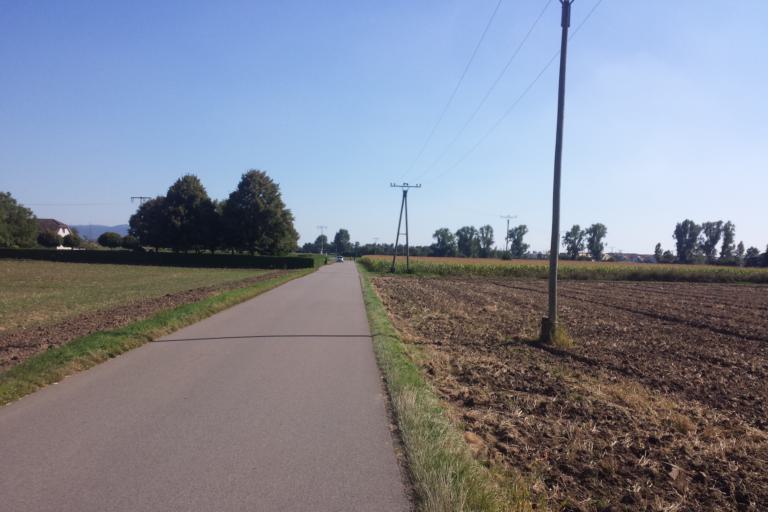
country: DE
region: Hesse
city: Viernheim
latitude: 49.5606
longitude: 8.6007
